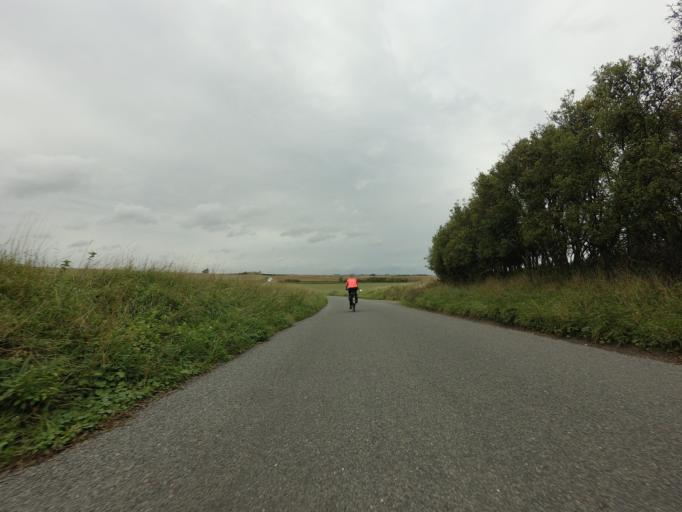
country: GB
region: England
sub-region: Cambridgeshire
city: Duxford
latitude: 52.0407
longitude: 0.1739
